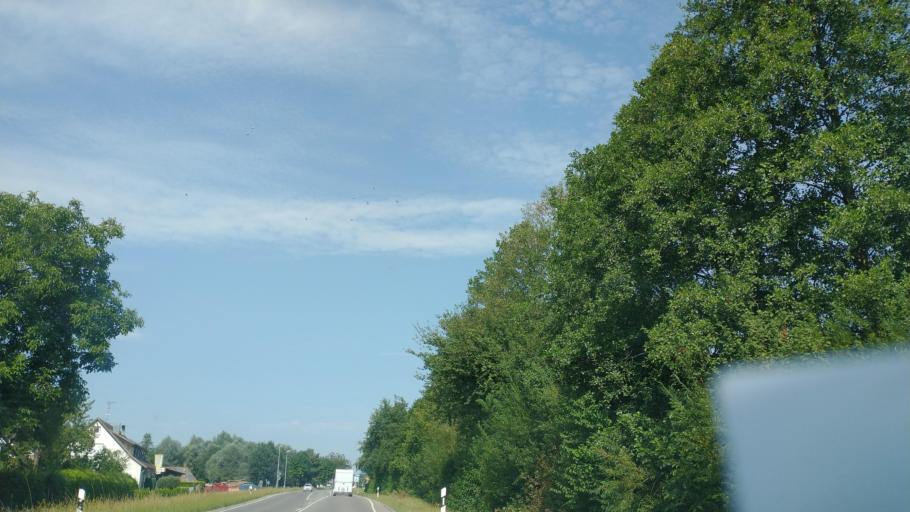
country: DE
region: Baden-Wuerttemberg
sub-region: Tuebingen Region
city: Tettnang
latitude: 47.6670
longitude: 9.5658
